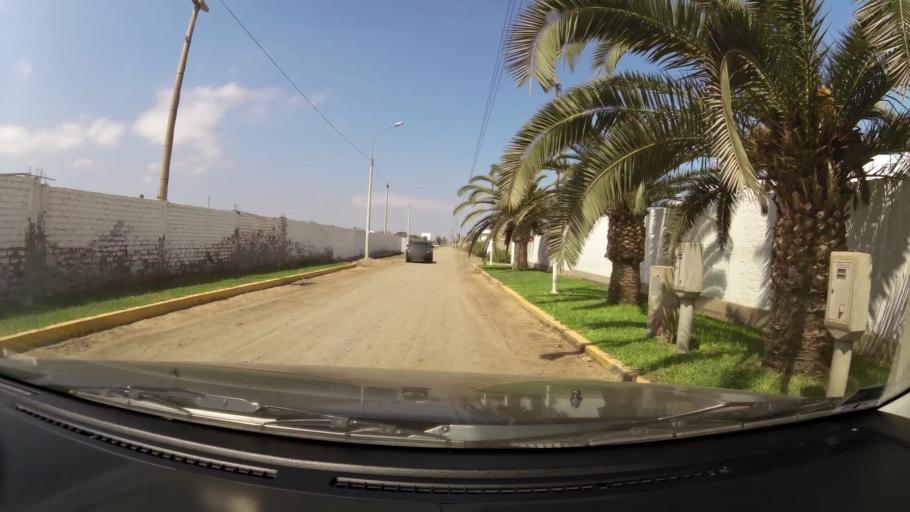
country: PE
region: Lima
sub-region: Provincia de Canete
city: Mala
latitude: -12.6801
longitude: -76.6537
